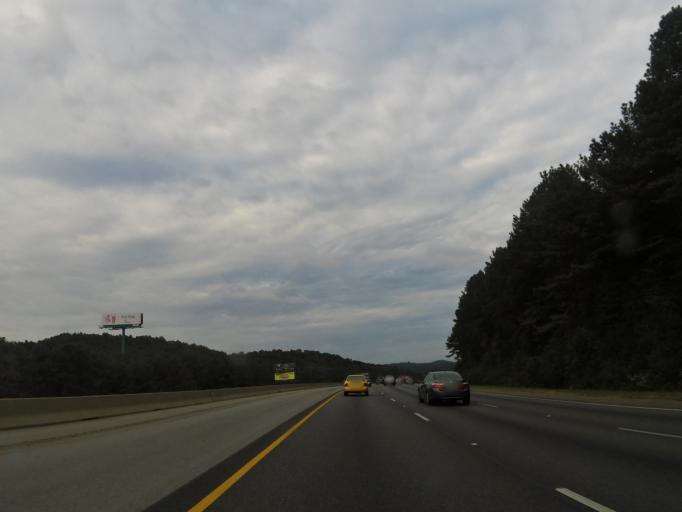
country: US
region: Alabama
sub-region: Shelby County
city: Pelham
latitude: 33.3209
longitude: -86.7865
